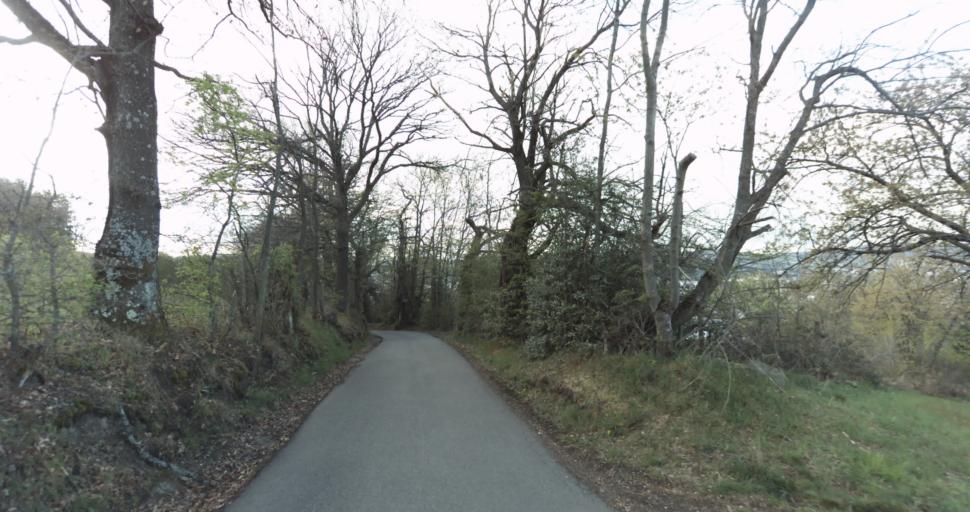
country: FR
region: Rhone-Alpes
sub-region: Departement de la Loire
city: Sorbiers
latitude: 45.4776
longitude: 4.4542
